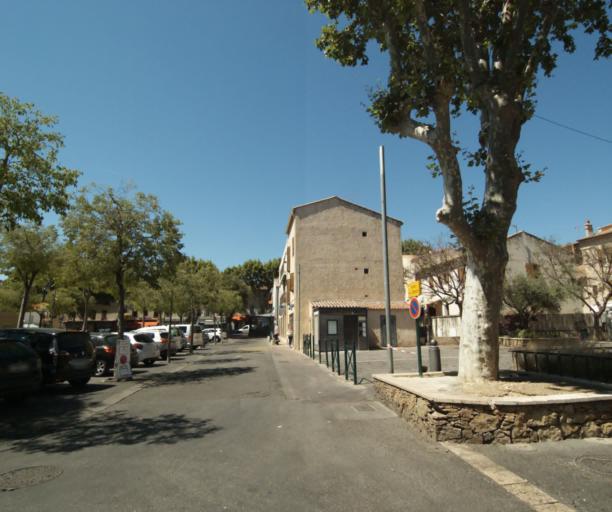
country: FR
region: Provence-Alpes-Cote d'Azur
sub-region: Departement du Var
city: La Garde
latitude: 43.1243
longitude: 6.0103
